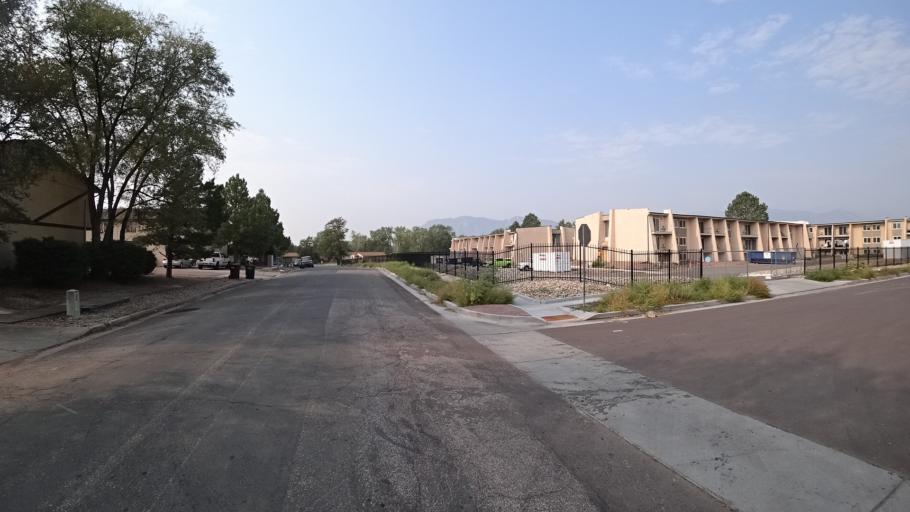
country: US
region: Colorado
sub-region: El Paso County
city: Stratmoor
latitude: 38.8068
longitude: -104.7751
